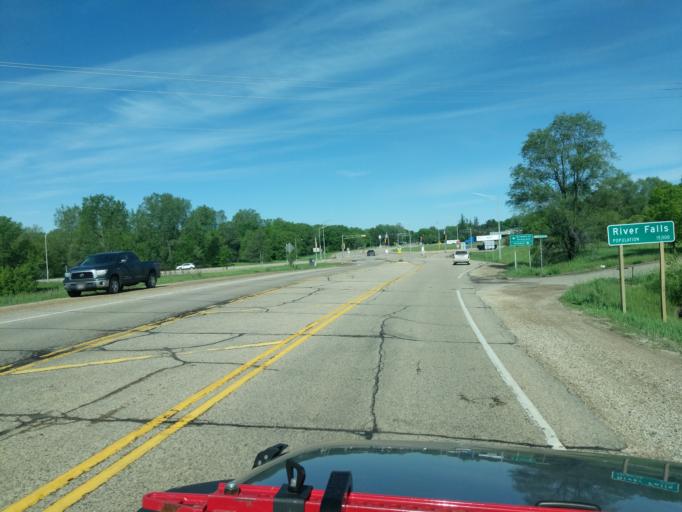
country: US
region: Wisconsin
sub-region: Pierce County
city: River Falls
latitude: 44.8499
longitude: -92.6035
